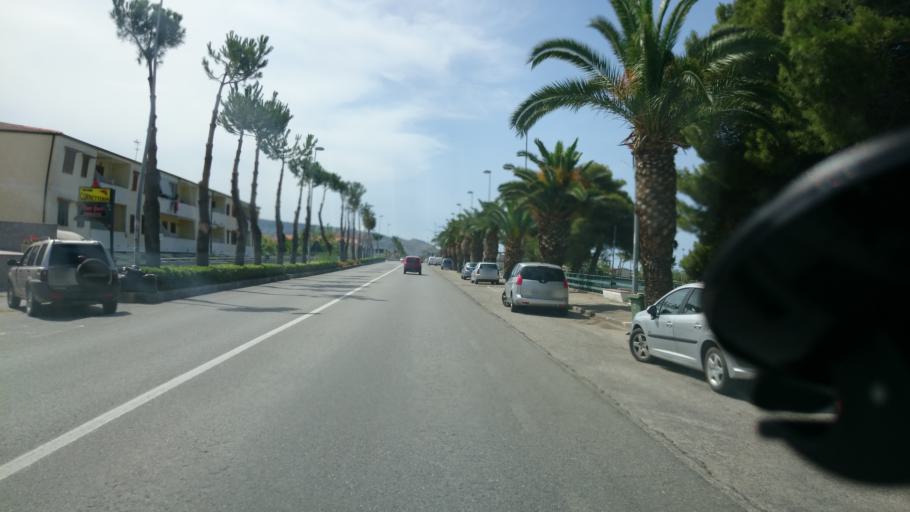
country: IT
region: Calabria
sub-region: Provincia di Cosenza
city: Marcellina
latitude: 39.7595
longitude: 15.8023
